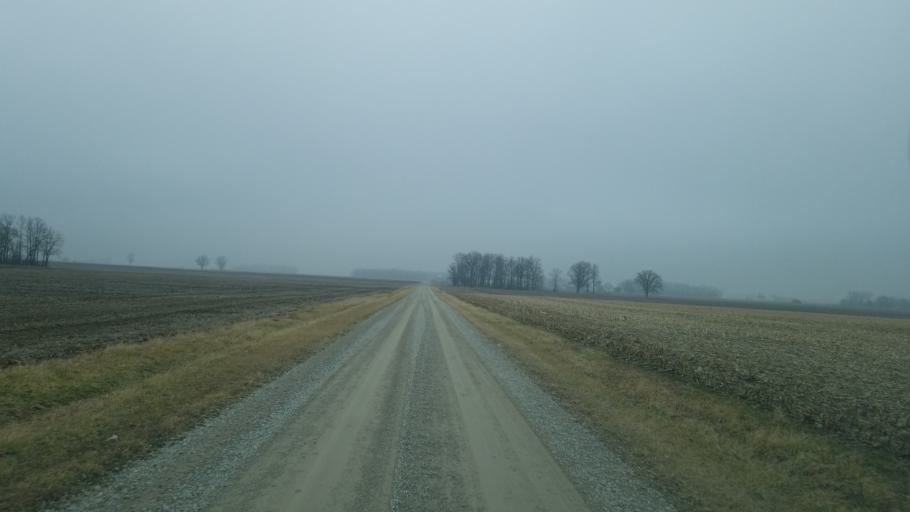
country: US
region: Indiana
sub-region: Adams County
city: Geneva
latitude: 40.6315
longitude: -85.0699
